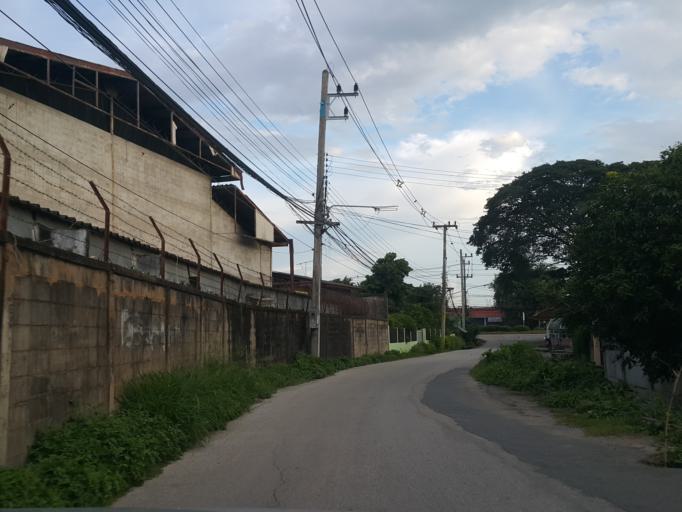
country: TH
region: Chiang Mai
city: San Sai
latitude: 18.8585
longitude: 99.1022
